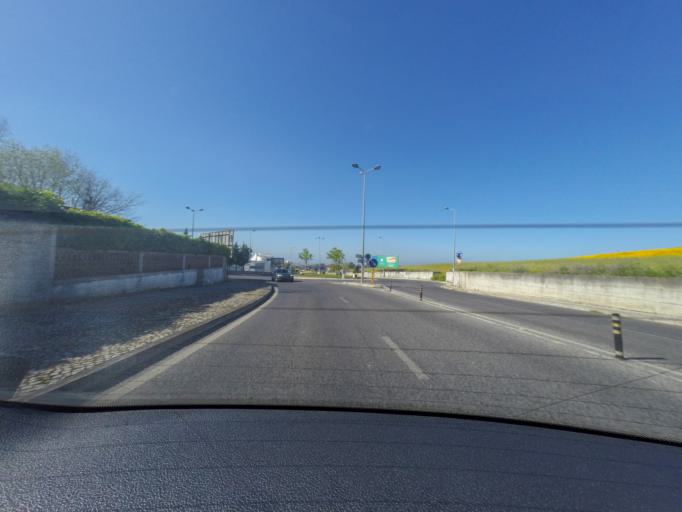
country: PT
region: Lisbon
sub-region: Cascais
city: Alcabideche
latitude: 38.7622
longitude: -9.3864
